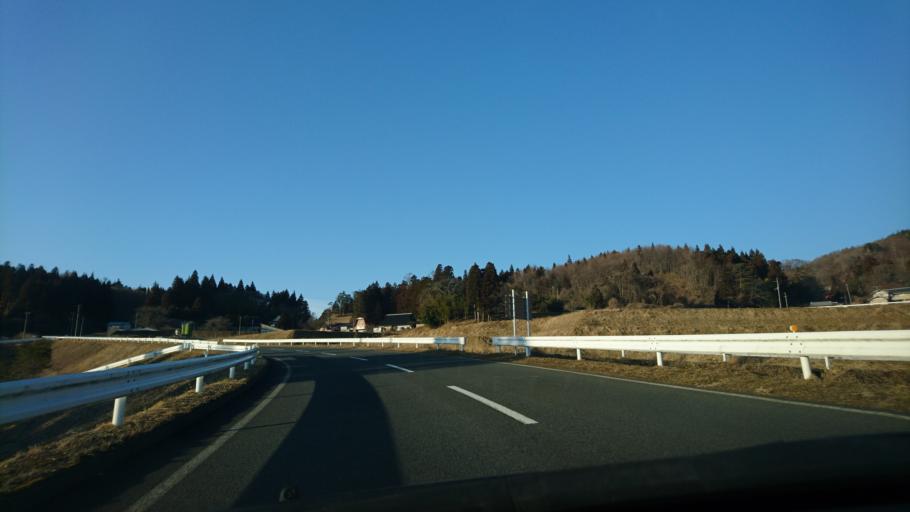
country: JP
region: Iwate
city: Mizusawa
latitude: 39.0255
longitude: 141.3754
